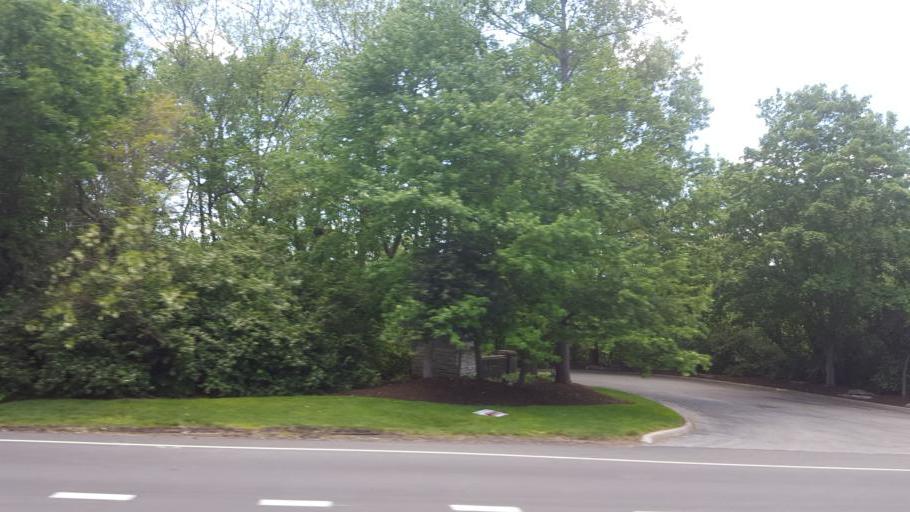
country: US
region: Ohio
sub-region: Franklin County
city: Dublin
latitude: 40.0971
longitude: -83.1085
